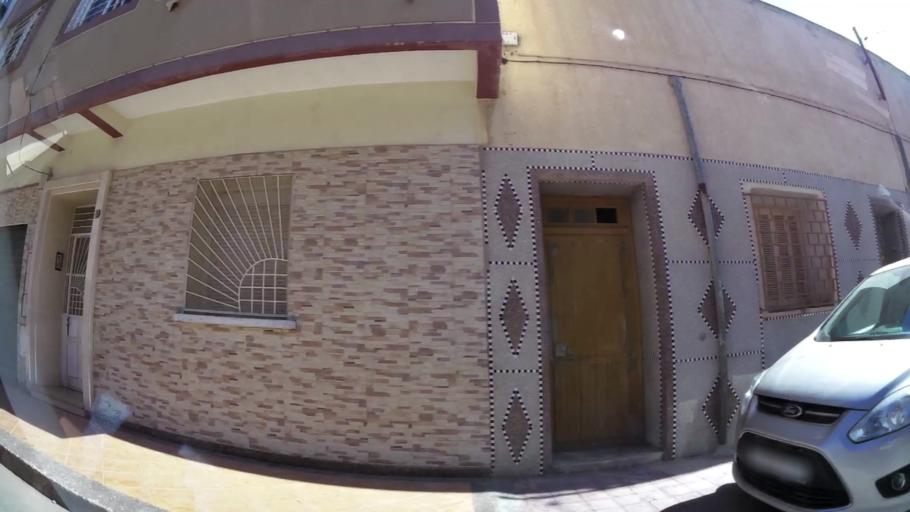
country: MA
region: Oriental
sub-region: Oujda-Angad
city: Oujda
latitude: 34.6942
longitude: -1.9197
